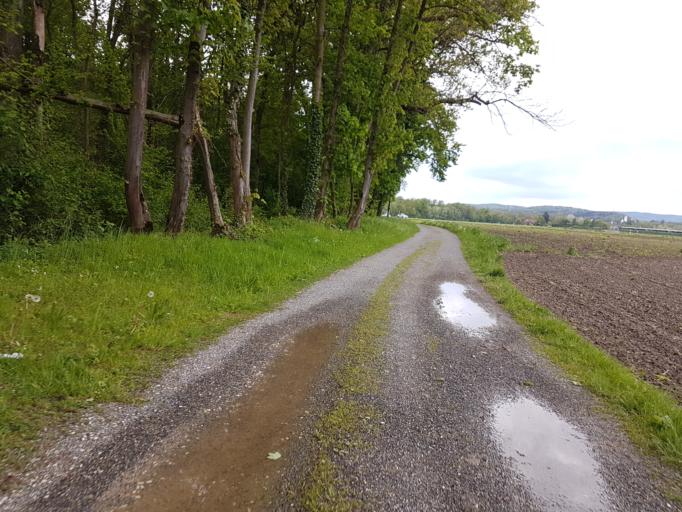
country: CH
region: Aargau
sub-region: Bezirk Brugg
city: Lauffohr (Brugg)
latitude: 47.4993
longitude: 8.2333
